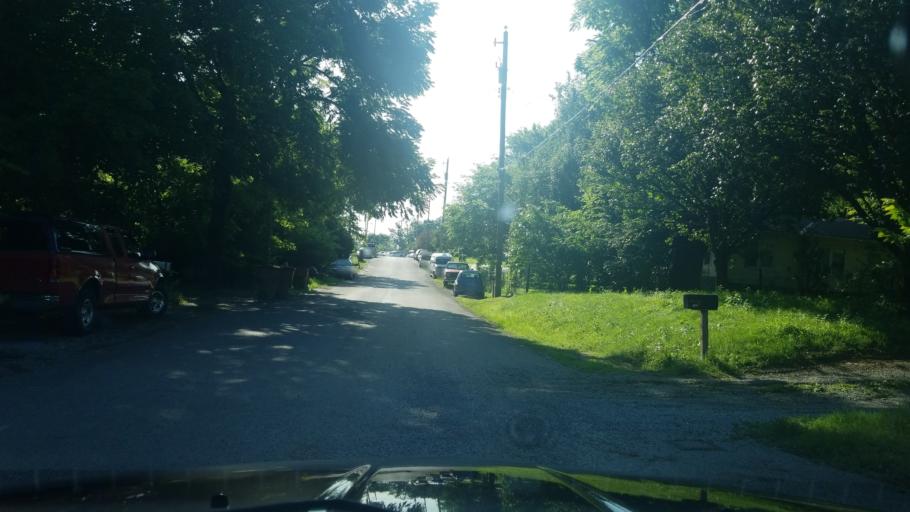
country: US
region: Tennessee
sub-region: Davidson County
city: Oak Hill
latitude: 36.1052
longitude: -86.7448
